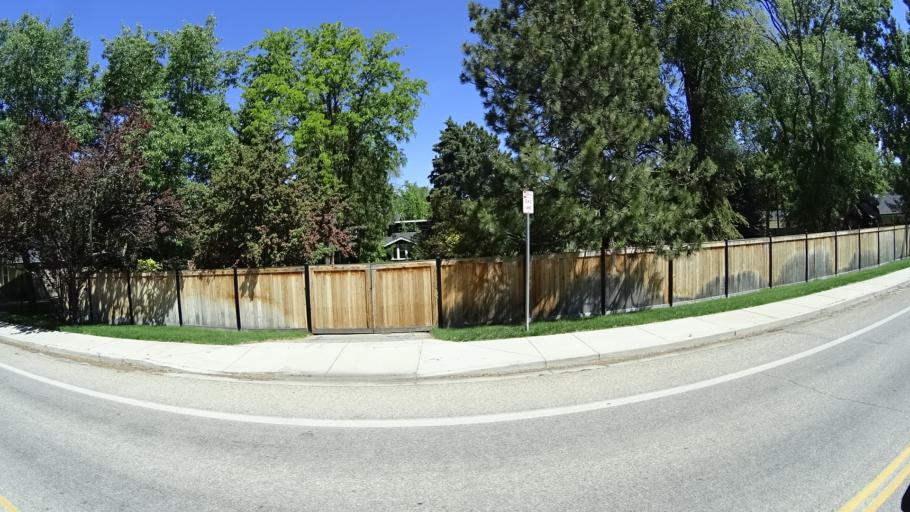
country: US
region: Idaho
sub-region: Ada County
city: Boise
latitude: 43.5860
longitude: -116.1751
